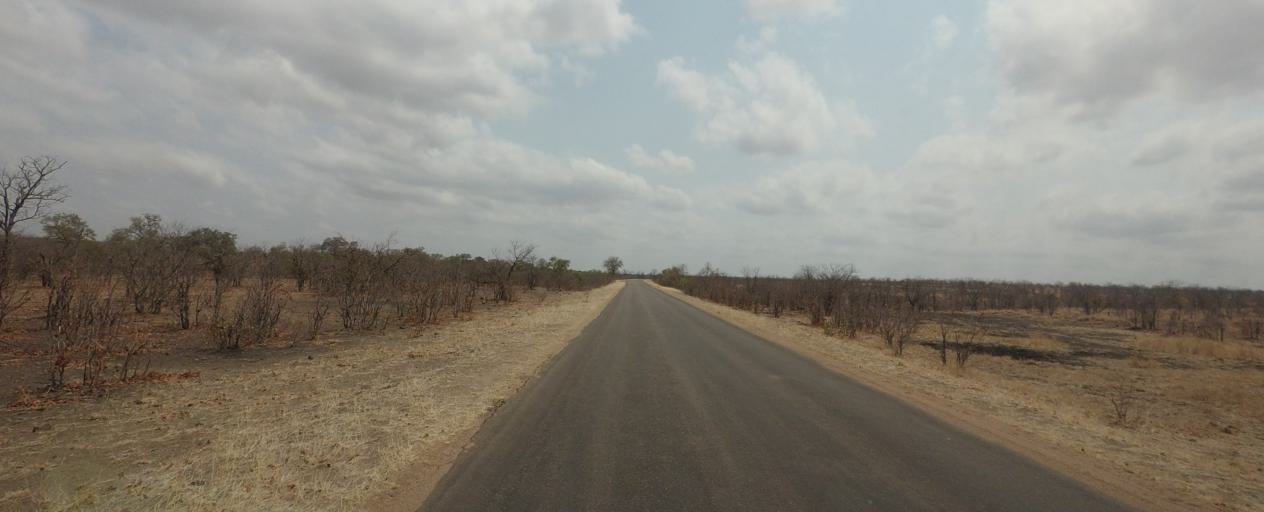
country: ZA
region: Limpopo
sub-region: Mopani District Municipality
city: Phalaborwa
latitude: -23.5907
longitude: 31.4527
